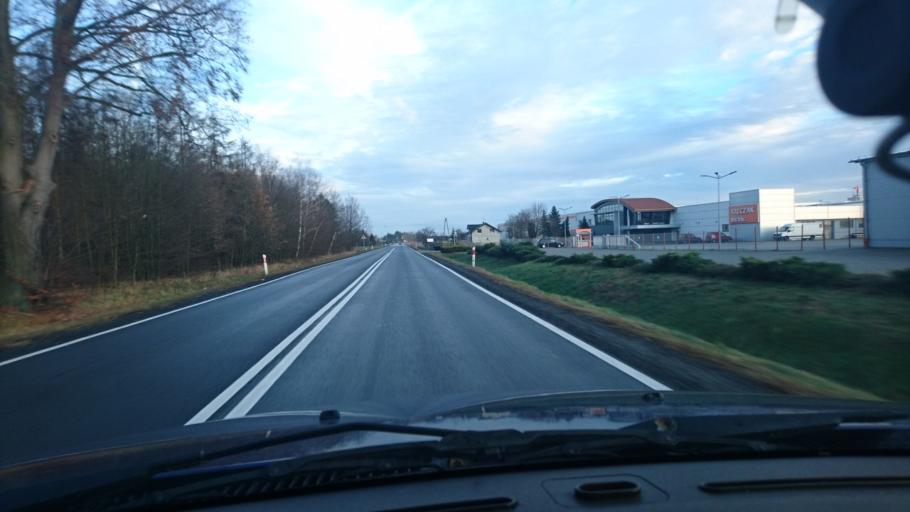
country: PL
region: Greater Poland Voivodeship
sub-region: Powiat kepinski
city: Leka Opatowska
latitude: 51.2248
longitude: 18.0974
